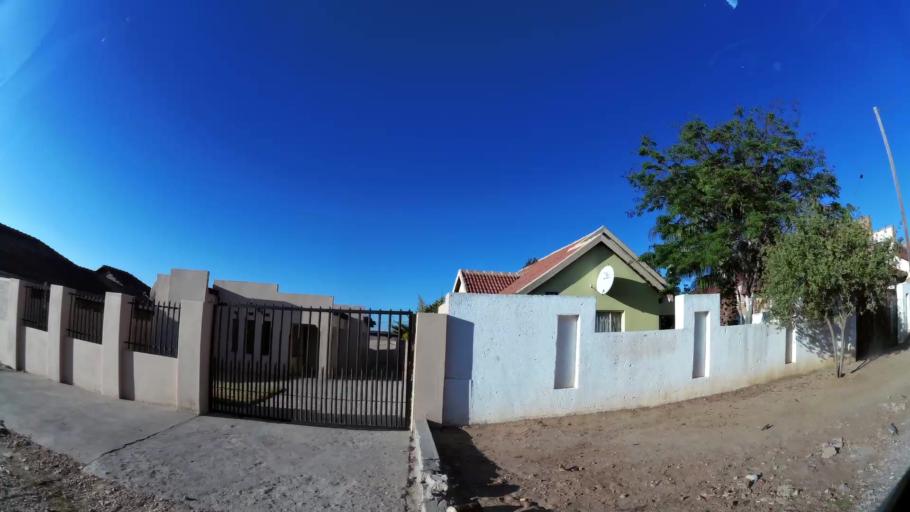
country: ZA
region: Limpopo
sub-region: Capricorn District Municipality
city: Polokwane
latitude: -23.8463
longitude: 29.3553
